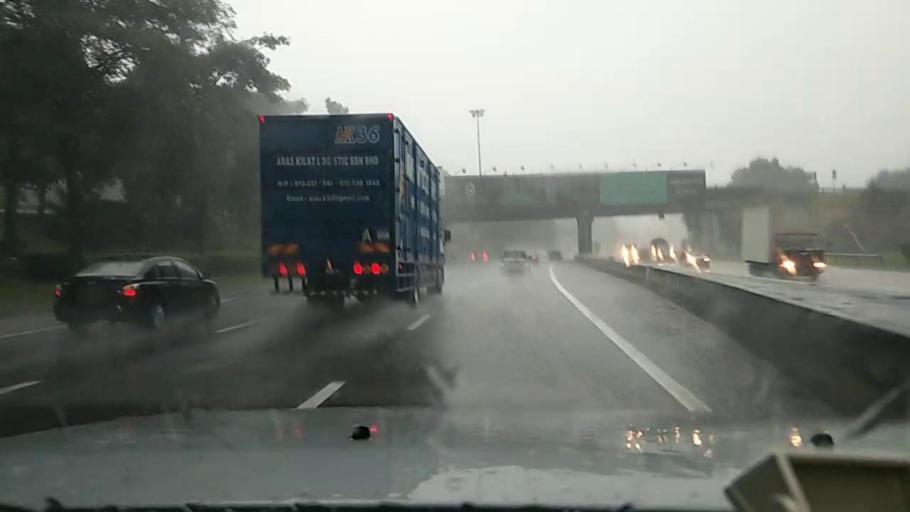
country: MY
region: Selangor
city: Kampong Baharu Balakong
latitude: 2.9823
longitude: 101.7478
